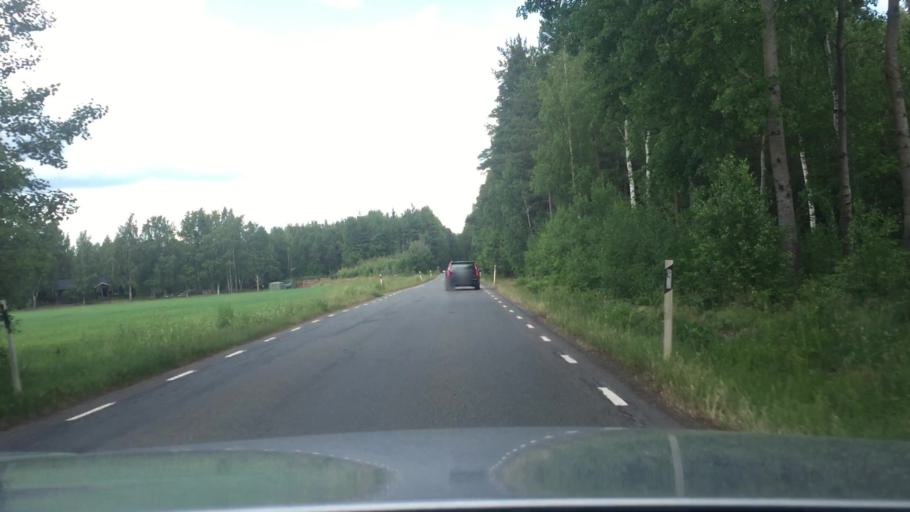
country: SE
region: Vaestra Goetaland
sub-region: Tidaholms Kommun
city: Tidaholm
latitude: 58.1987
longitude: 13.9790
